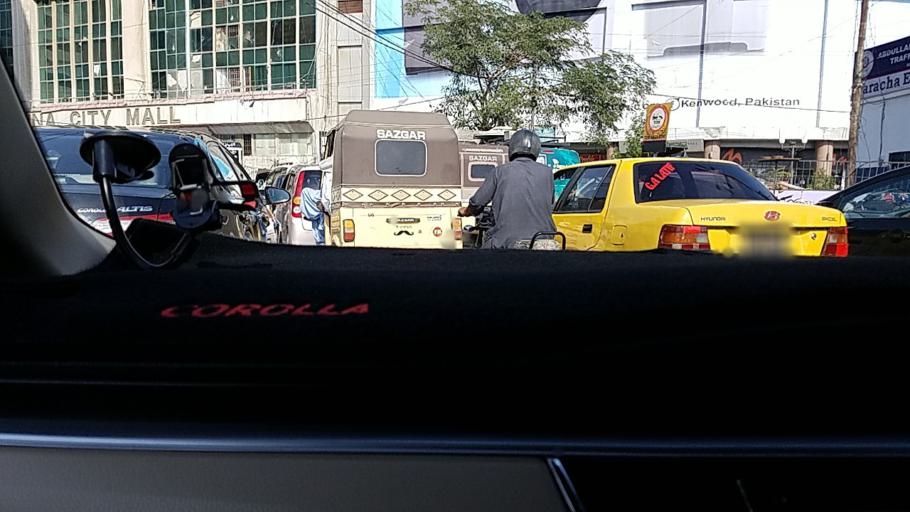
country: PK
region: Sindh
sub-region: Karachi District
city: Karachi
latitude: 24.8541
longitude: 67.0284
